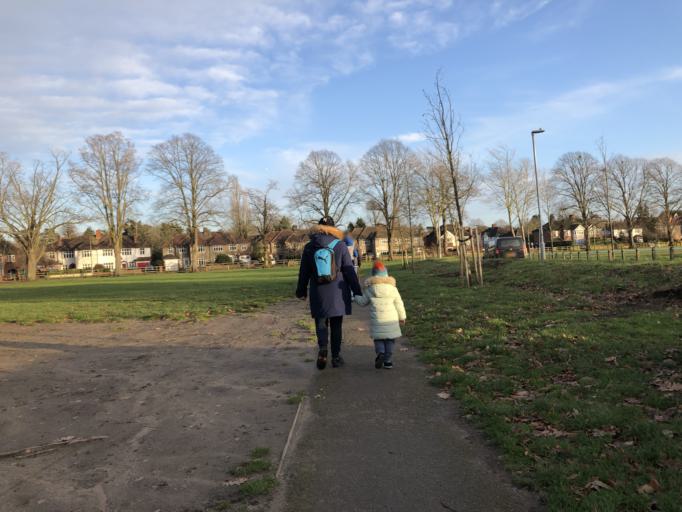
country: GB
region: England
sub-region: Reading
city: Reading
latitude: 51.4505
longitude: -1.0054
